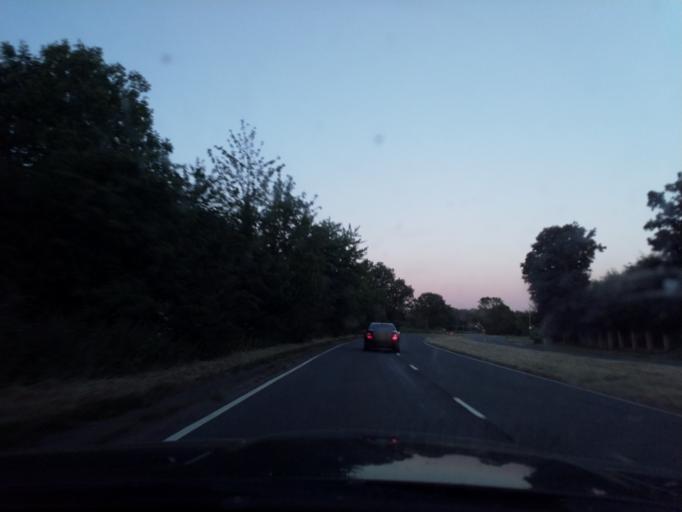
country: GB
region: England
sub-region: Solihull
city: Balsall Common
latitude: 52.4106
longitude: -1.6677
